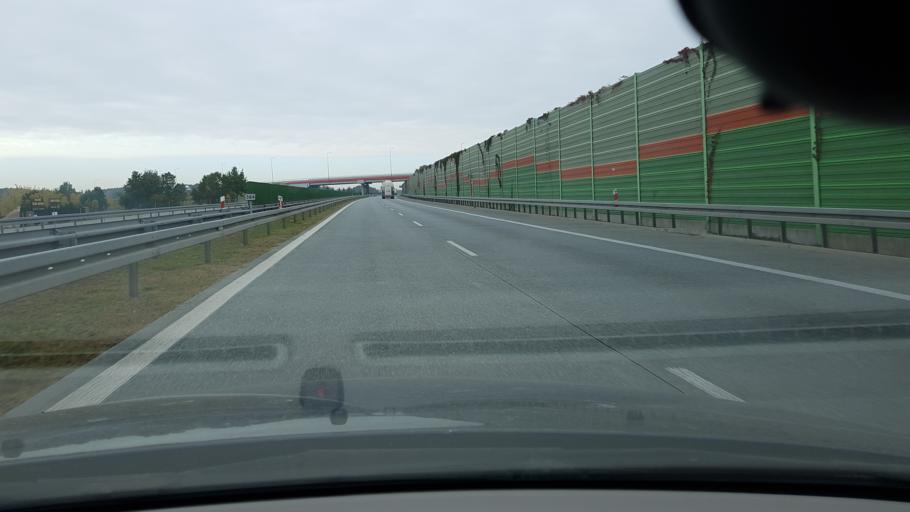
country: PL
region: Lodz Voivodeship
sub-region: Powiat rawski
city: Rawa Mazowiecka
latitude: 51.7578
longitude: 20.2600
